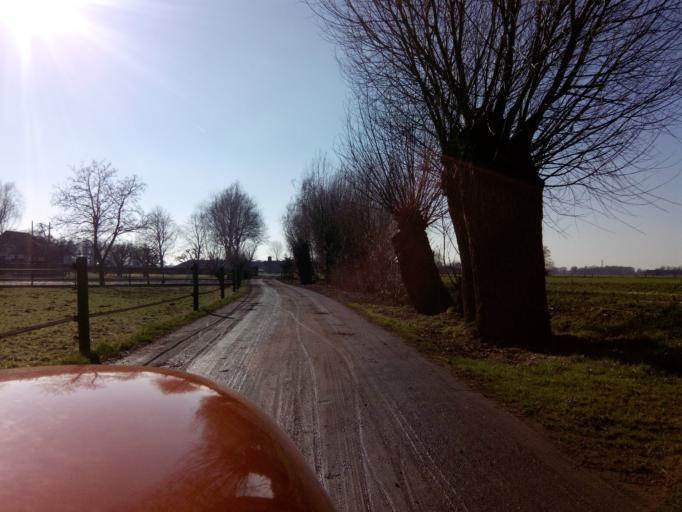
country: NL
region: Gelderland
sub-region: Gemeente Barneveld
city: Barneveld
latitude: 52.1276
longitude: 5.5443
